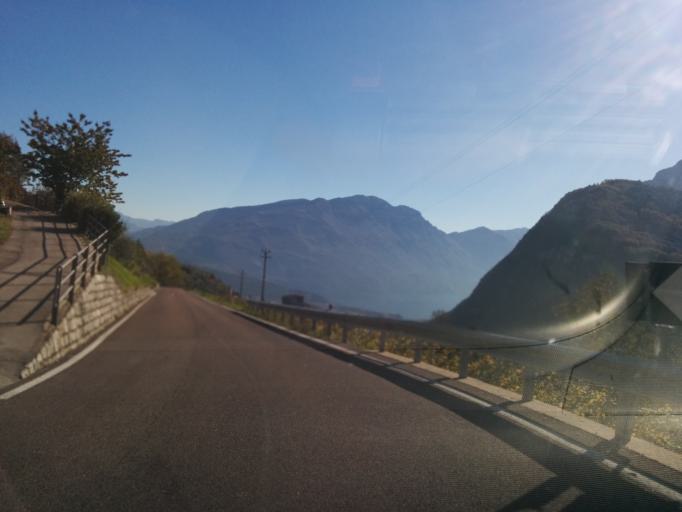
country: IT
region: Trentino-Alto Adige
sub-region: Provincia di Trento
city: Tenno
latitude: 45.9283
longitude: 10.8248
